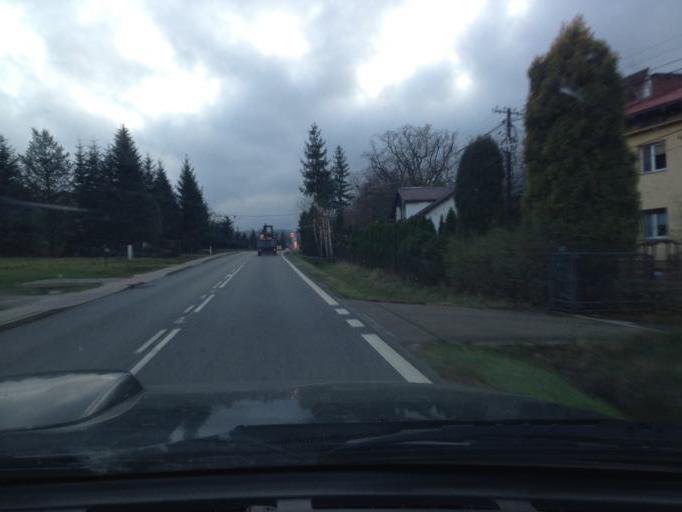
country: PL
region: Subcarpathian Voivodeship
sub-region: Powiat jasielski
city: Nowy Zmigrod
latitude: 49.6106
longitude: 21.5306
